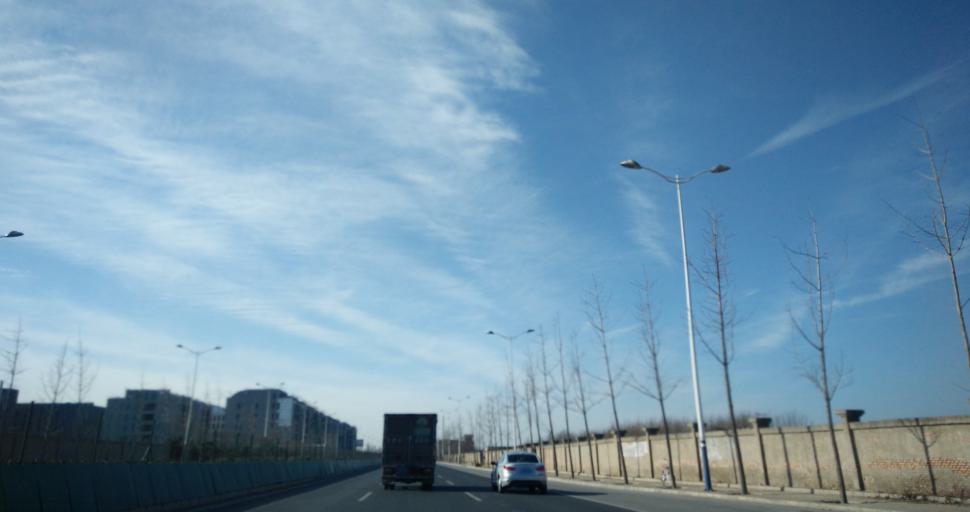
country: CN
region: Beijing
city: Yinghai
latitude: 39.7395
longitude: 116.4201
